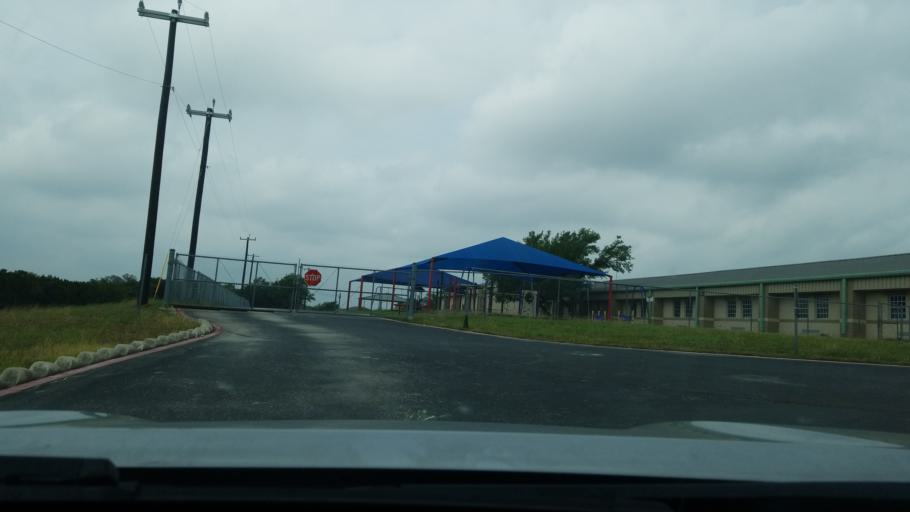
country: US
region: Texas
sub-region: Bexar County
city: Timberwood Park
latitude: 29.6834
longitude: -98.4593
